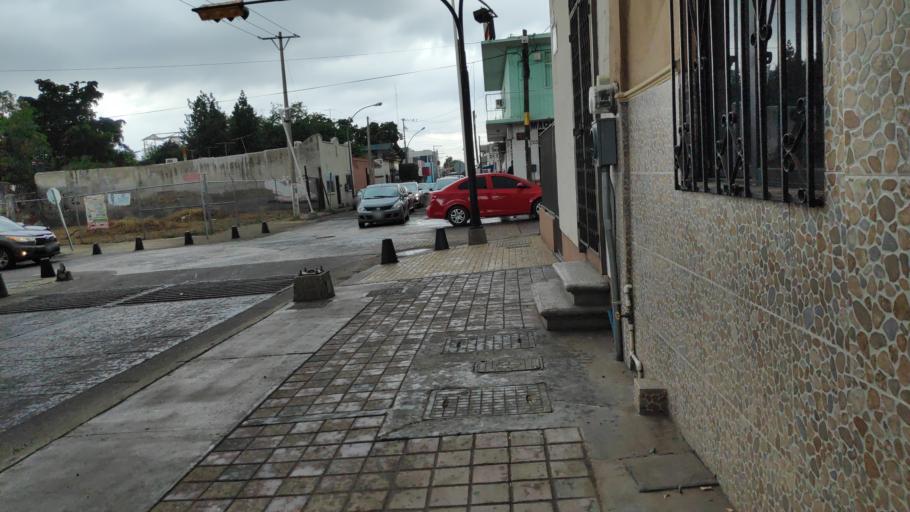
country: MX
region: Sinaloa
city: Culiacan
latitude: 24.8062
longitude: -107.4007
